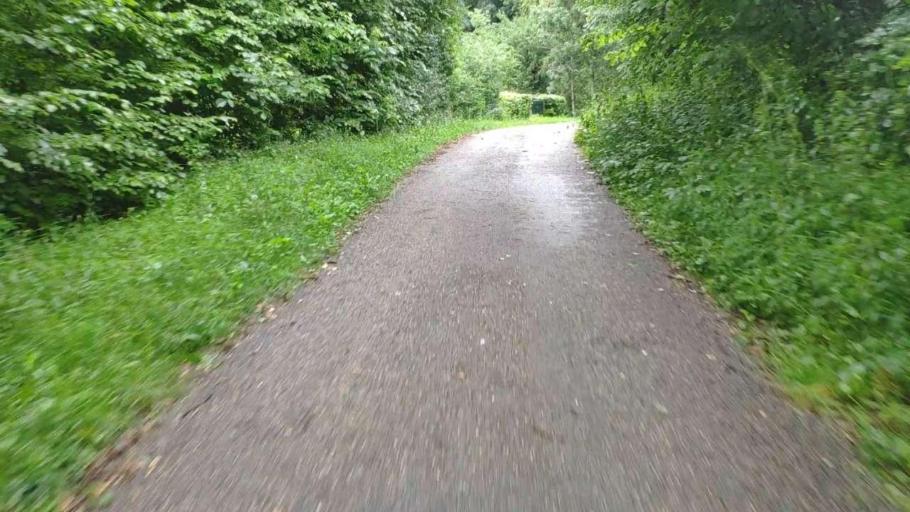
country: FR
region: Franche-Comte
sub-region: Departement du Jura
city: Poligny
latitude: 46.7841
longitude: 5.6221
